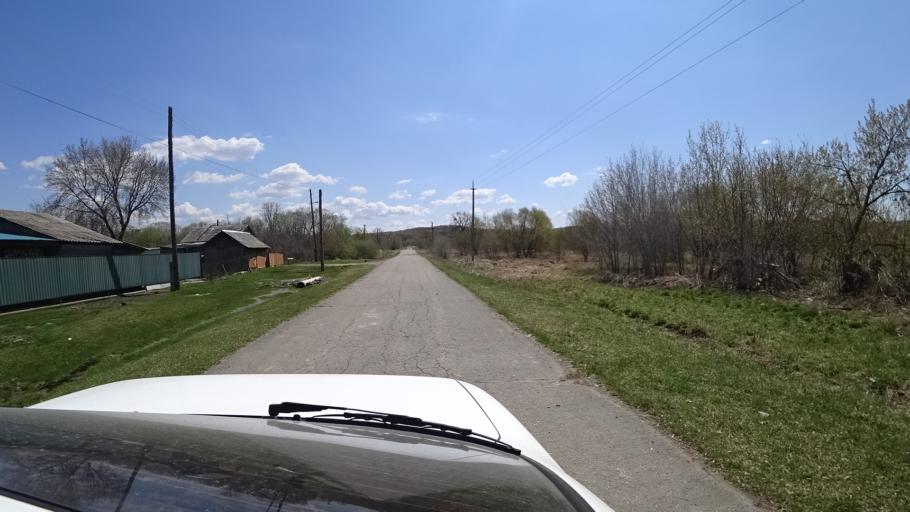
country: RU
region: Primorskiy
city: Lazo
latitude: 45.7910
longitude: 133.7676
